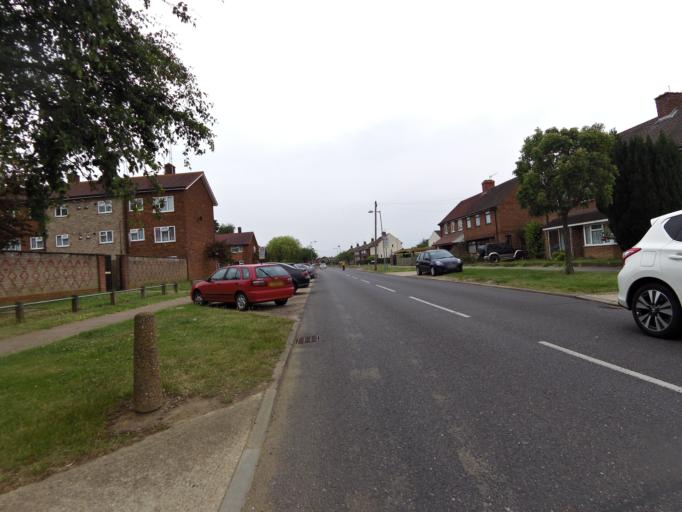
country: GB
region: England
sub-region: Suffolk
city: Ipswich
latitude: 52.0845
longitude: 1.1355
